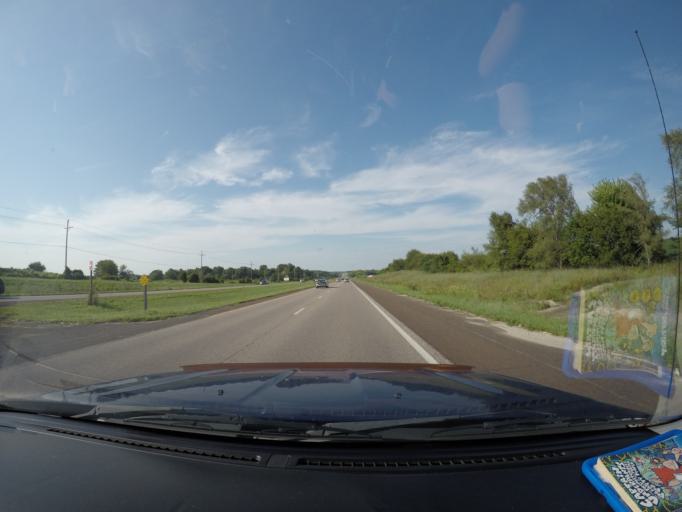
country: US
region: Kansas
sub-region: Leavenworth County
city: Lansing
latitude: 39.2129
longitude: -94.9001
